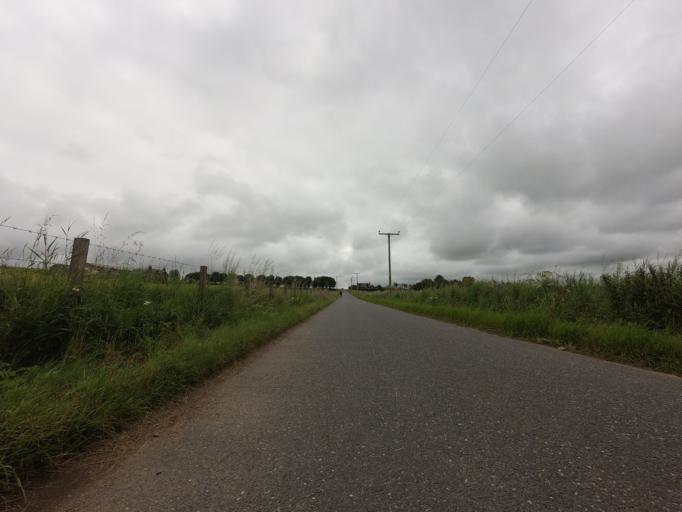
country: GB
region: Scotland
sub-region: Aberdeenshire
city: Turriff
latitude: 57.5354
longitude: -2.4336
